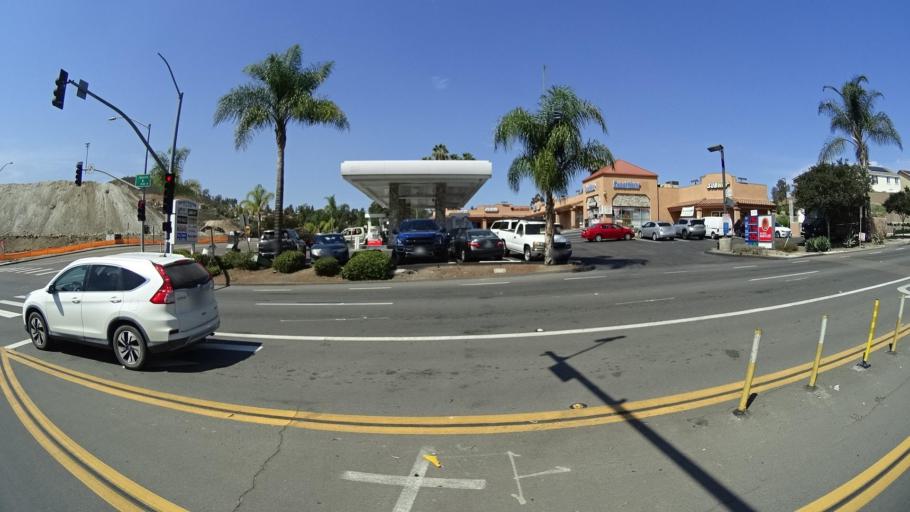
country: US
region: California
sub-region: San Diego County
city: La Presa
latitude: 32.7258
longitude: -116.9687
